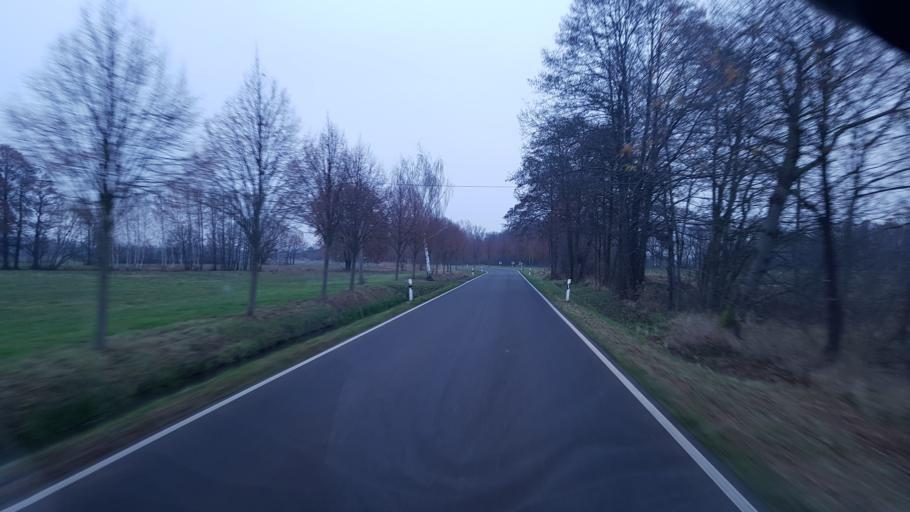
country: DE
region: Brandenburg
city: Werben
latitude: 51.8456
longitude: 14.1816
